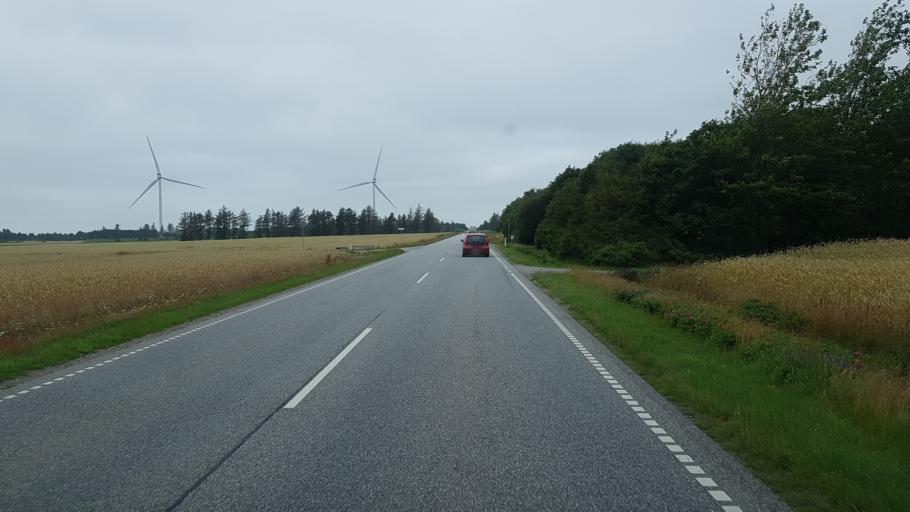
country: DK
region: Central Jutland
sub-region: Lemvig Kommune
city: Lemvig
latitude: 56.4432
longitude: 8.3618
